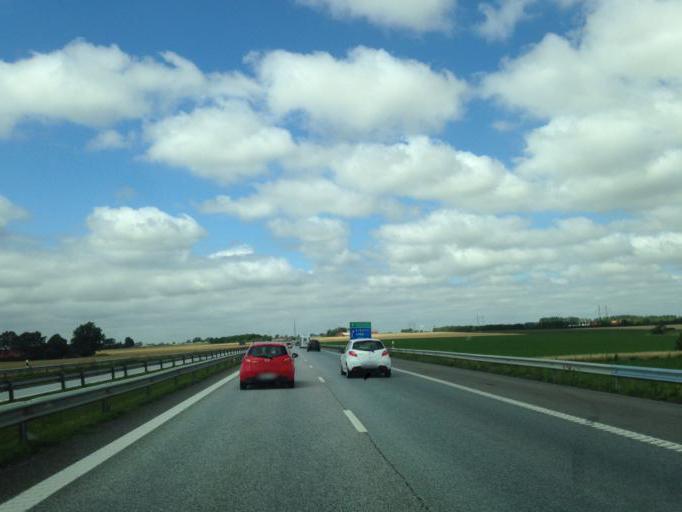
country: SE
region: Skane
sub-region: Lomma Kommun
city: Lomma
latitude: 55.7135
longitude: 13.0940
